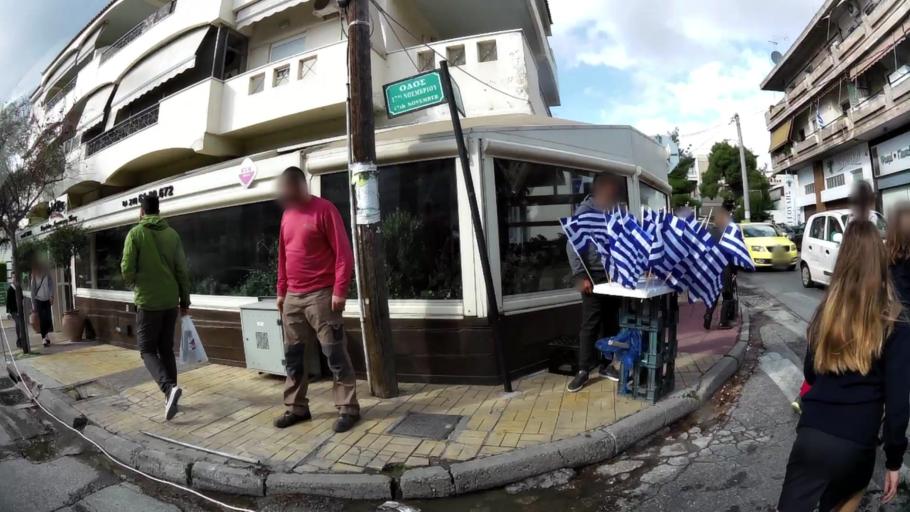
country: GR
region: Attica
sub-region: Nomarchia Athinas
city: Melissia
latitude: 38.0607
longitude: 23.8363
